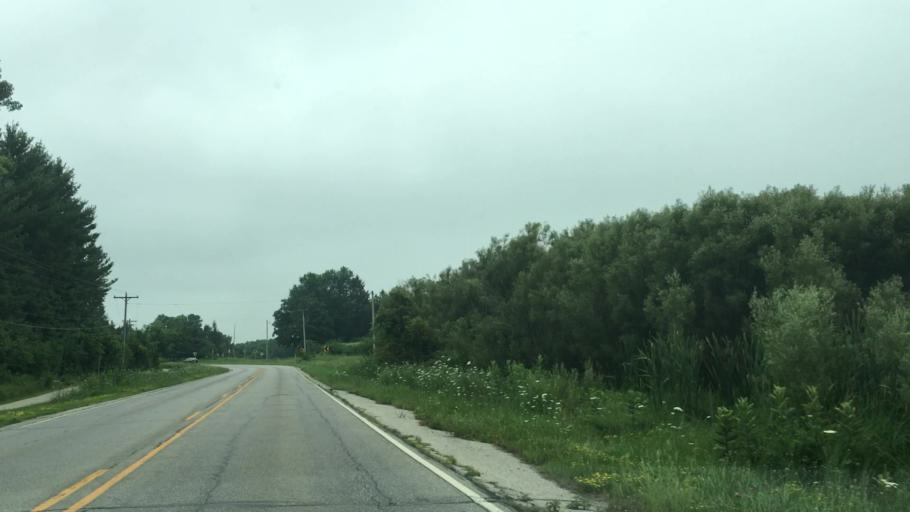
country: US
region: Iowa
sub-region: Johnson County
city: North Liberty
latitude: 41.7240
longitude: -91.5610
